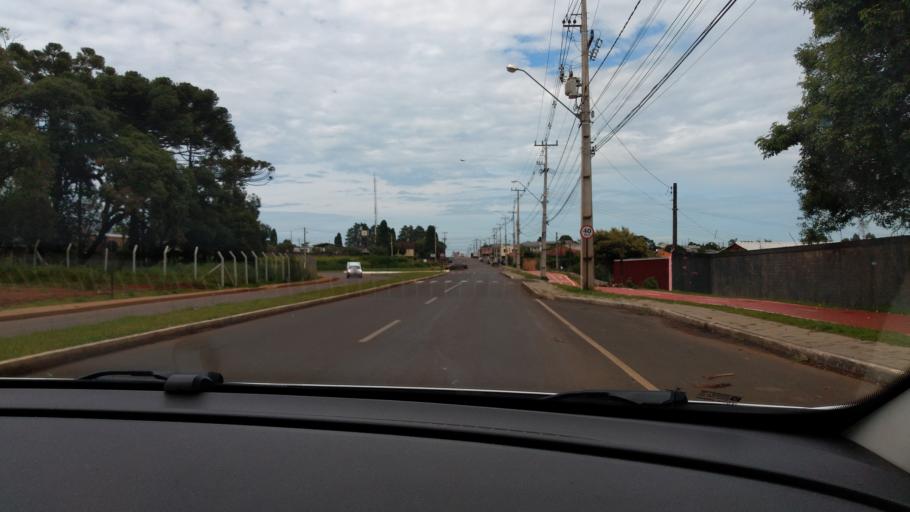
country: BR
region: Parana
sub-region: Guarapuava
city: Guarapuava
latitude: -25.3707
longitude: -51.4408
